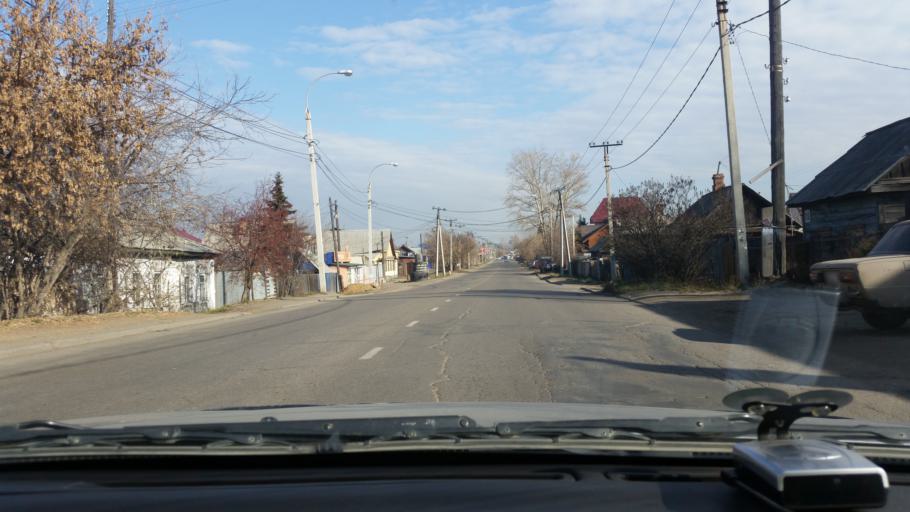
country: RU
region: Irkutsk
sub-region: Irkutskiy Rayon
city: Irkutsk
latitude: 52.2836
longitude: 104.3232
